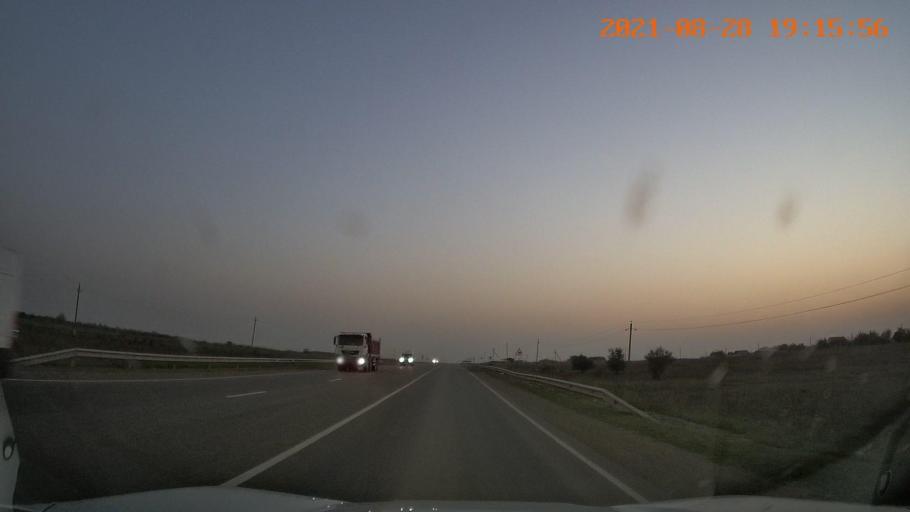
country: RU
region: Krasnodarskiy
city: Ryazanskaya
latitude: 44.9154
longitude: 39.5725
